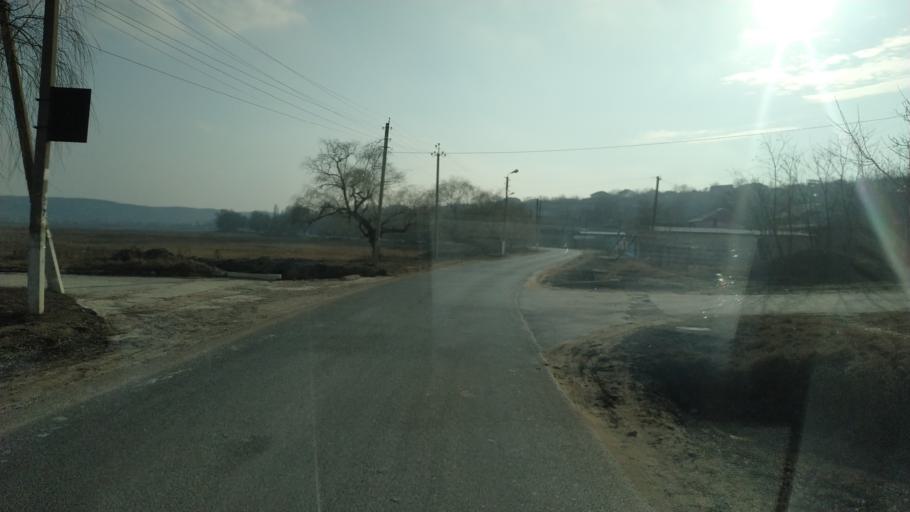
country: MD
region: Hincesti
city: Dancu
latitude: 46.7766
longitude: 28.3472
